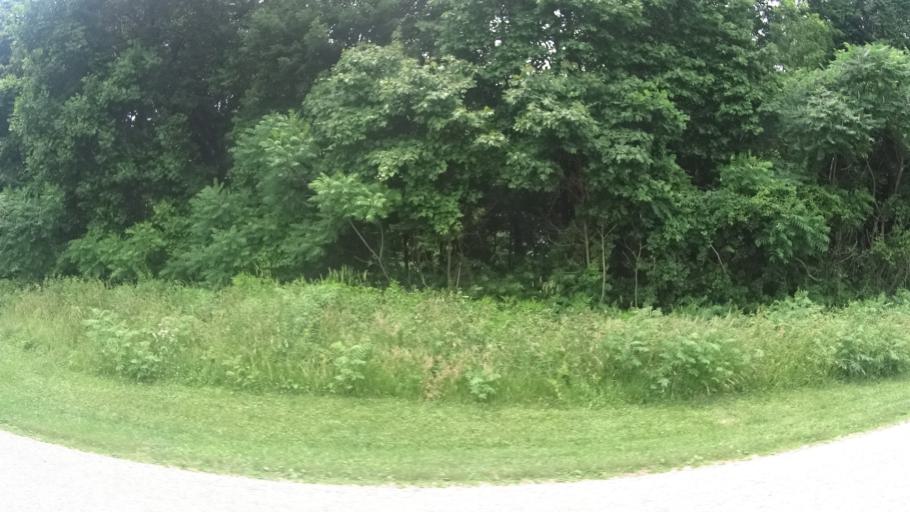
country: US
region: Ohio
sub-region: Erie County
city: Milan
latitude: 41.3030
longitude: -82.6318
